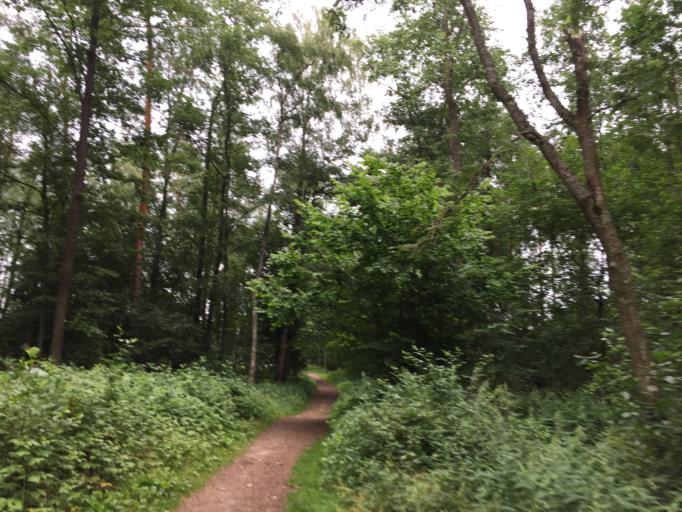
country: LV
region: Carnikava
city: Carnikava
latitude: 57.1192
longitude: 24.2228
